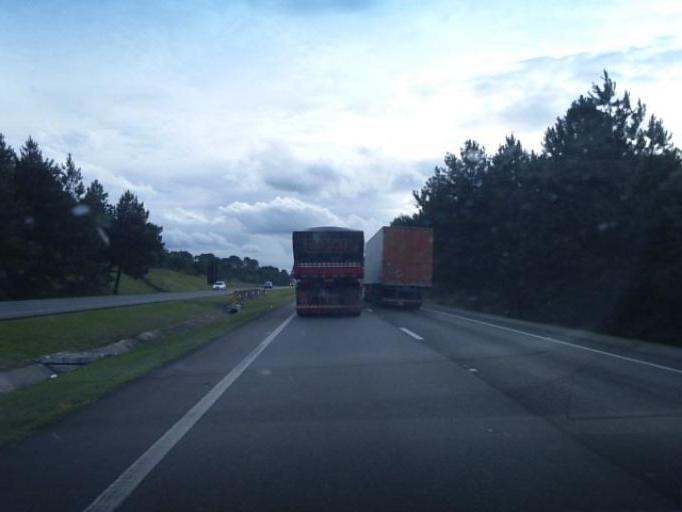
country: BR
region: Parana
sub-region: Piraquara
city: Piraquara
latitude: -25.4133
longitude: -49.0661
